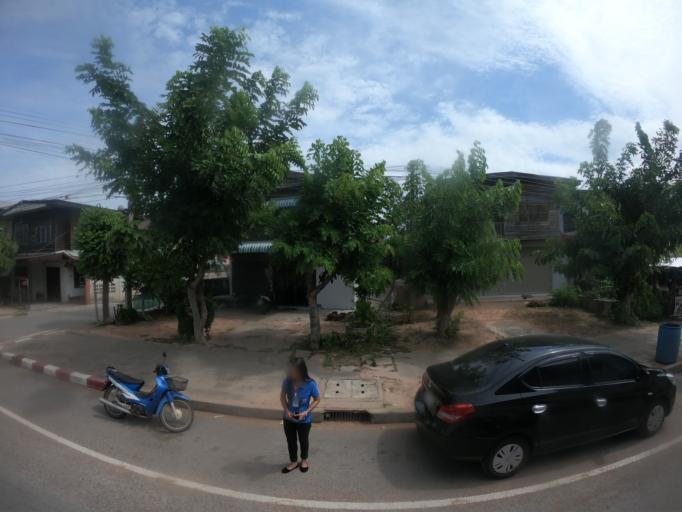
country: TH
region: Maha Sarakham
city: Chiang Yuen
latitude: 16.4073
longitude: 103.0983
